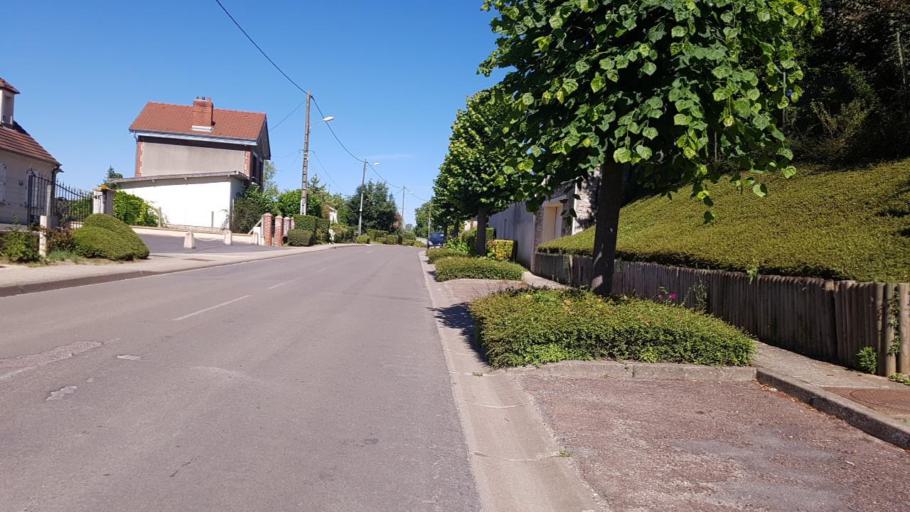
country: FR
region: Picardie
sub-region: Departement de l'Aisne
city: Charly-sur-Marne
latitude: 48.9727
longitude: 3.3132
